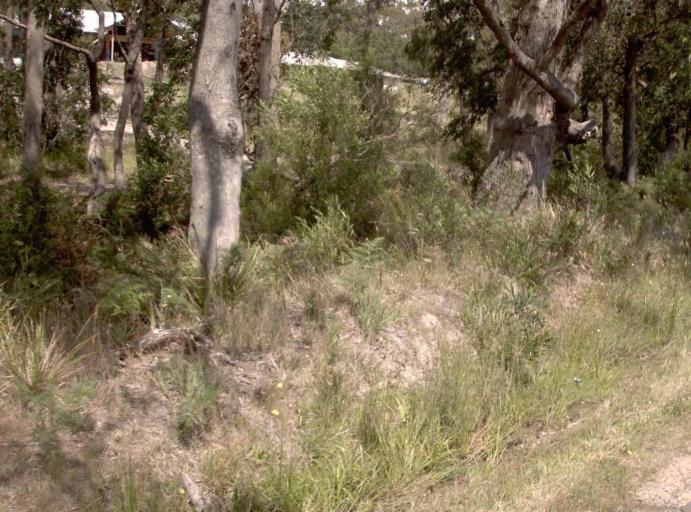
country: AU
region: Victoria
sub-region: Latrobe
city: Traralgon
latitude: -38.2999
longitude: 146.5384
